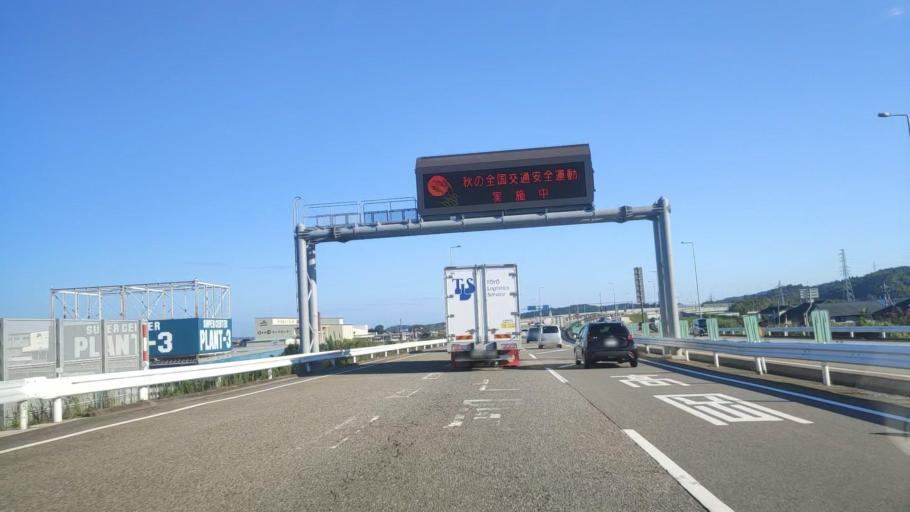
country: JP
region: Ishikawa
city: Tsubata
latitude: 36.6798
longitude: 136.7227
